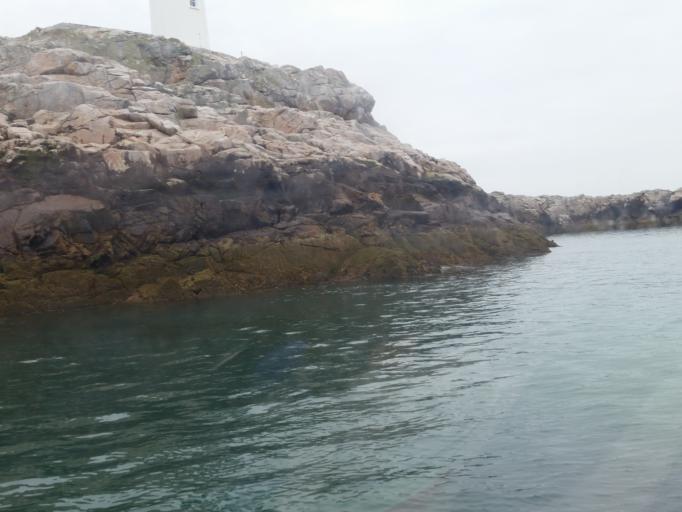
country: IE
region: Leinster
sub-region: Fingal County
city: Skerries
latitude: 53.5963
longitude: -6.0038
